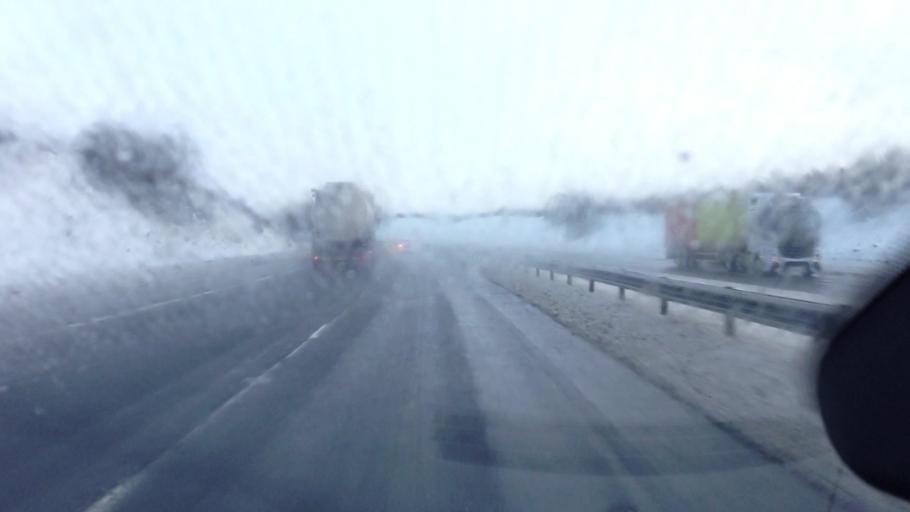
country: GB
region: Scotland
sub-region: South Lanarkshire
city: Blackwood
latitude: 55.6623
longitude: -3.9219
